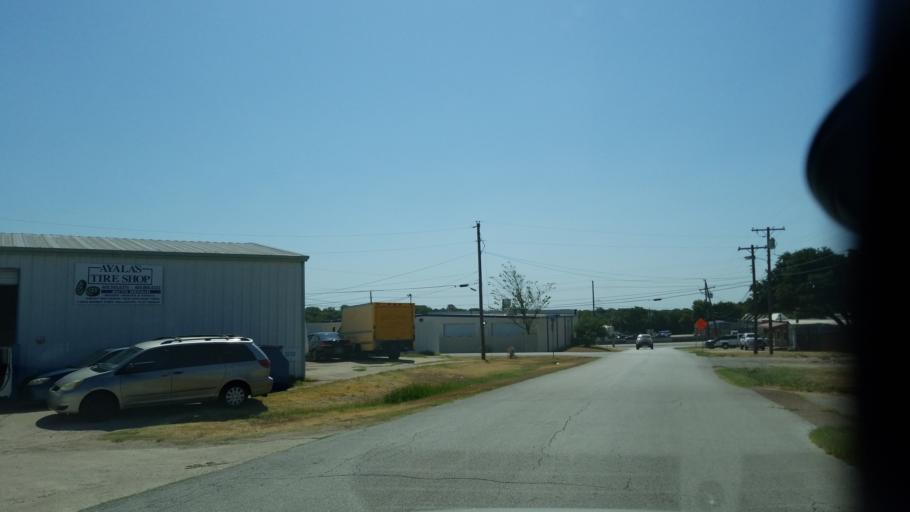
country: US
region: Texas
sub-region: Dallas County
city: Duncanville
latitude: 32.6387
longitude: -96.8967
